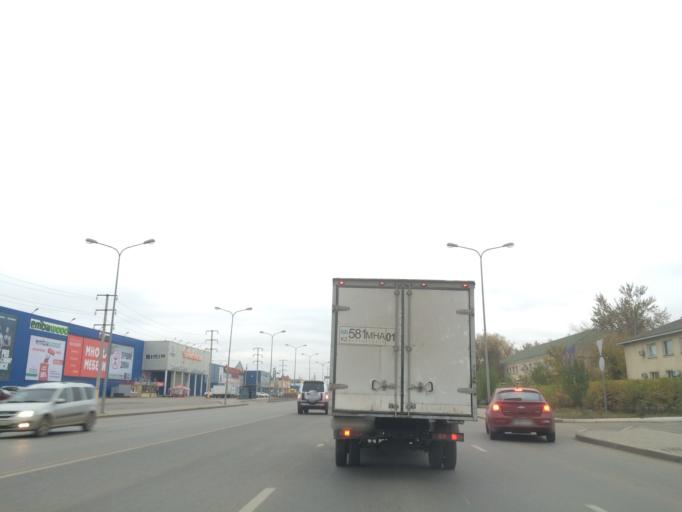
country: KZ
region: Astana Qalasy
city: Astana
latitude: 51.1821
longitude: 71.4587
